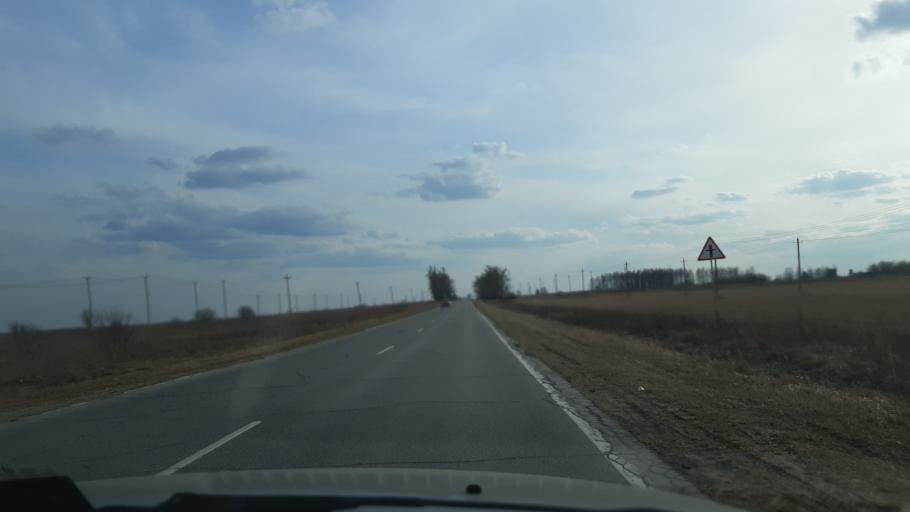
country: RU
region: Vladimir
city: Nikologory
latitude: 56.1685
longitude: 41.9994
